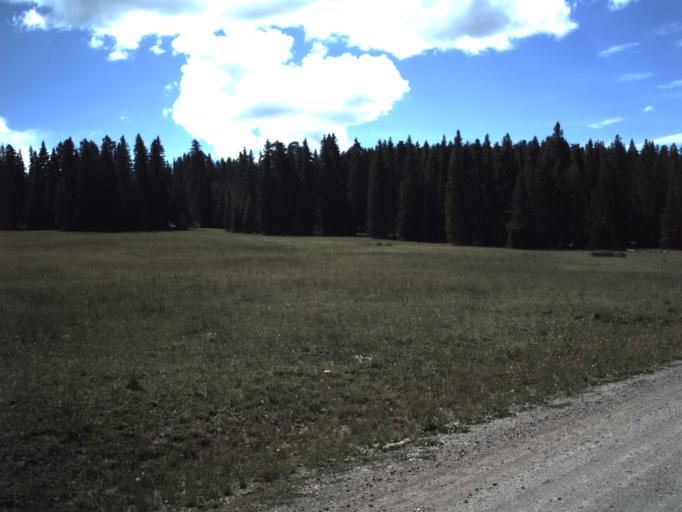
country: US
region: Utah
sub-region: Piute County
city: Junction
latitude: 38.2643
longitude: -112.3723
